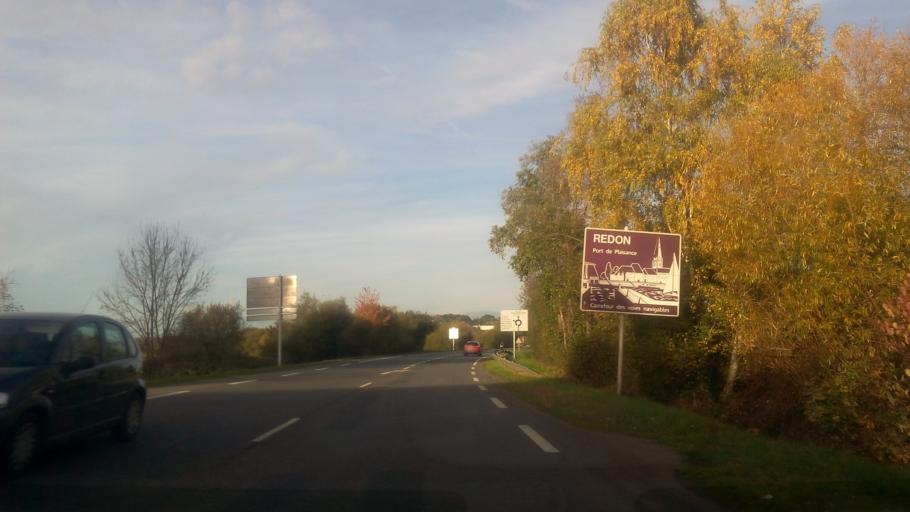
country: FR
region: Brittany
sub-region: Departement d'Ille-et-Vilaine
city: Redon
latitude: 47.6386
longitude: -2.1011
